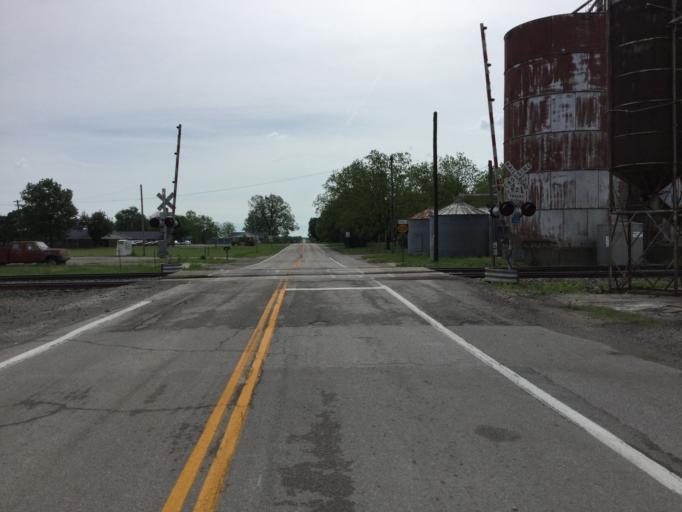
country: US
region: Kansas
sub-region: Linn County
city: Pleasanton
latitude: 38.0662
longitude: -94.6954
